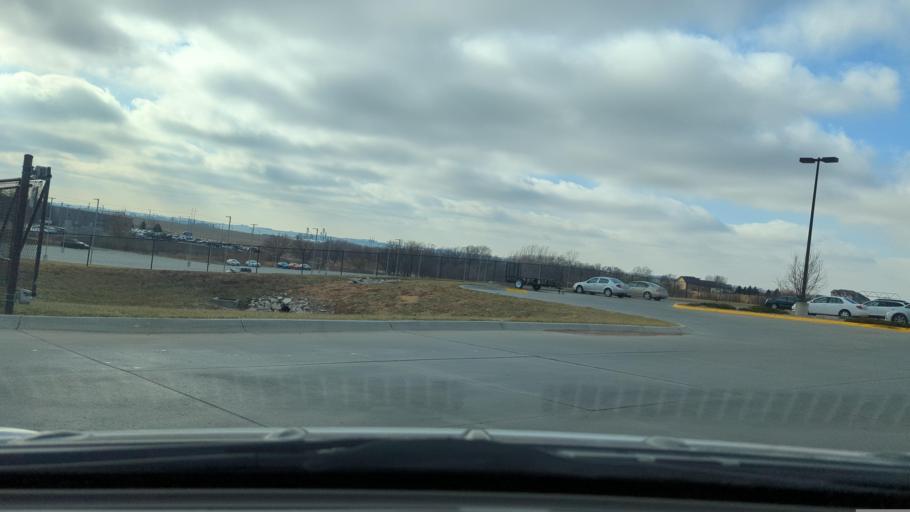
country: US
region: Nebraska
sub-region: Cass County
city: Plattsmouth
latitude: 40.9982
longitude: -95.9076
